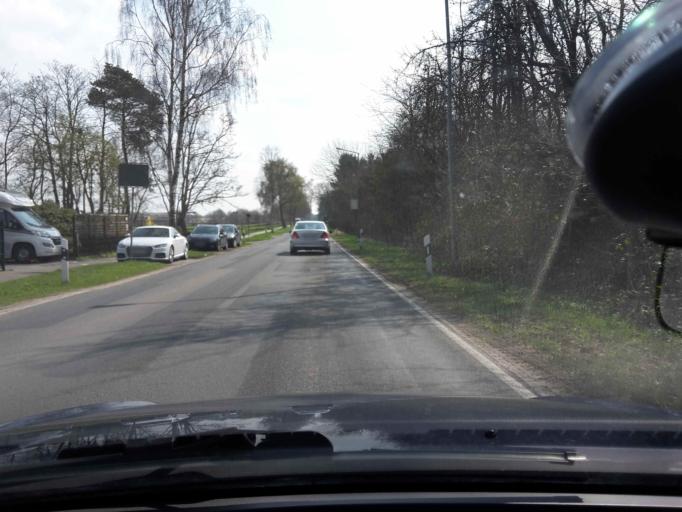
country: DE
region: Lower Saxony
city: Buchholz in der Nordheide
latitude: 53.3223
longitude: 9.8876
